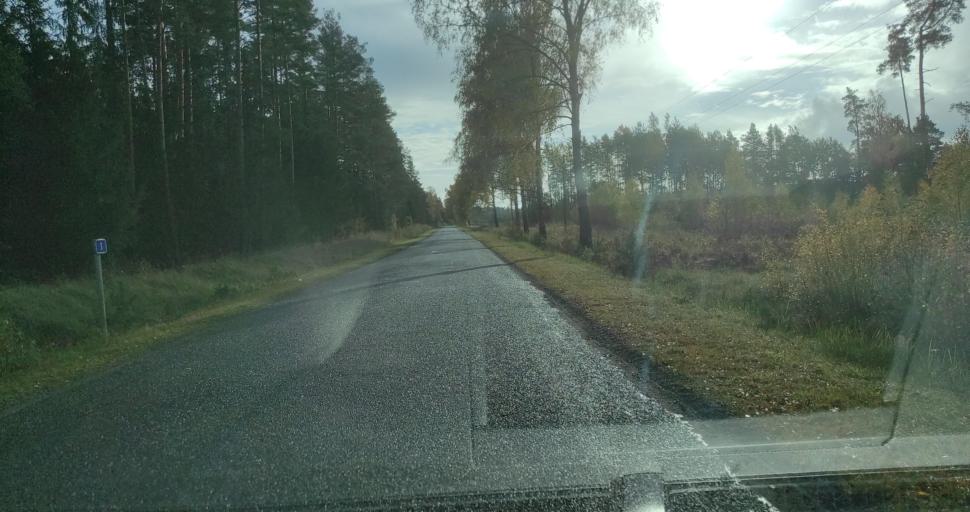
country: LV
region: Skrunda
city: Skrunda
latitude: 56.6847
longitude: 22.0604
